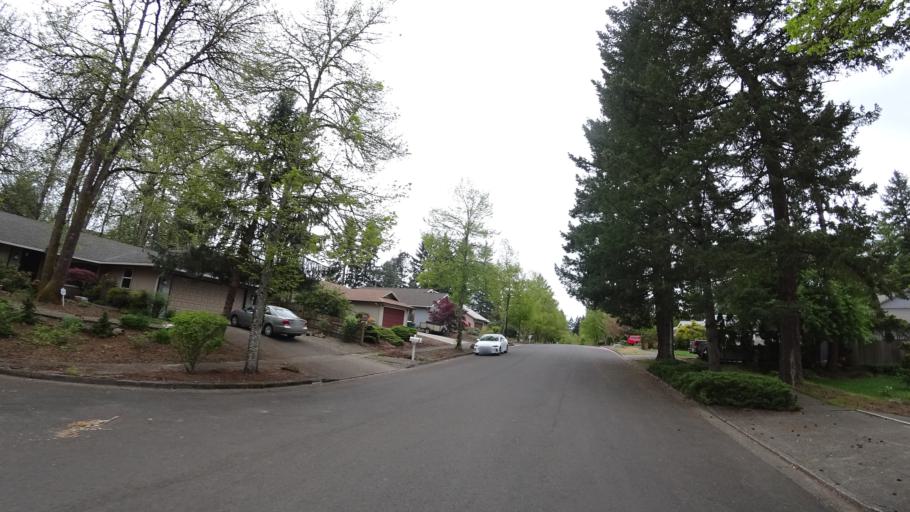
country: US
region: Oregon
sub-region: Washington County
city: Beaverton
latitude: 45.4626
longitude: -122.8269
